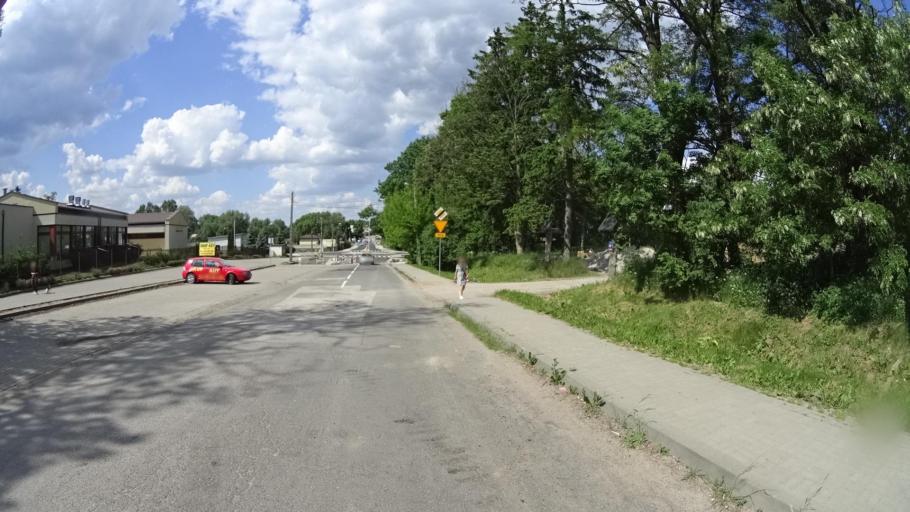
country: PL
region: Masovian Voivodeship
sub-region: Powiat piaseczynski
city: Tarczyn
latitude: 51.9746
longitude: 20.8336
